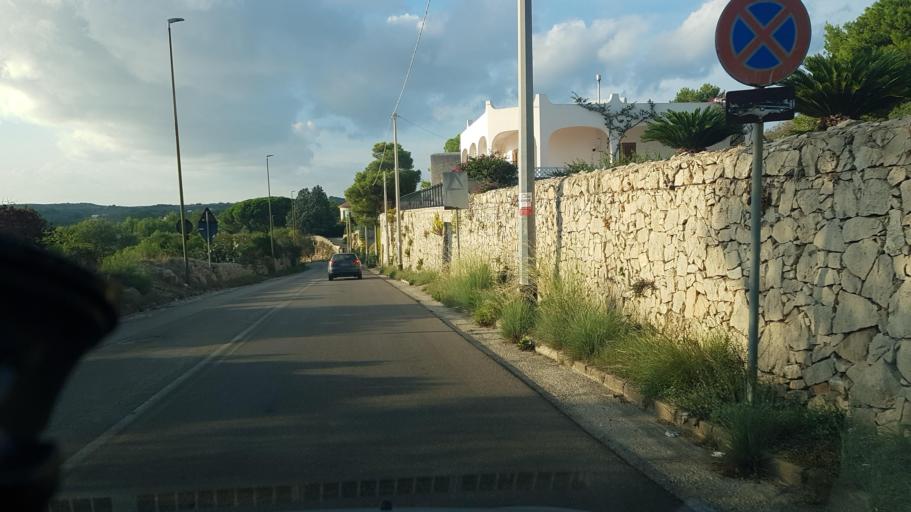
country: IT
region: Apulia
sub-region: Provincia di Lecce
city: Leuca
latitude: 39.7991
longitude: 18.3678
